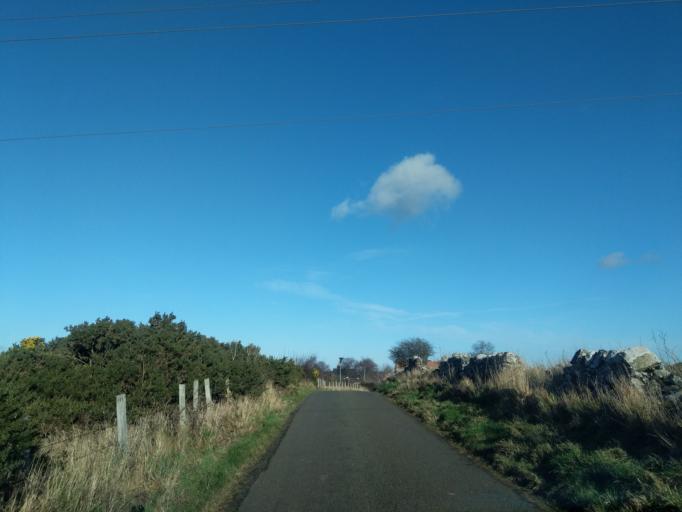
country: GB
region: Scotland
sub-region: East Lothian
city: East Linton
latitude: 55.9806
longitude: -2.6581
